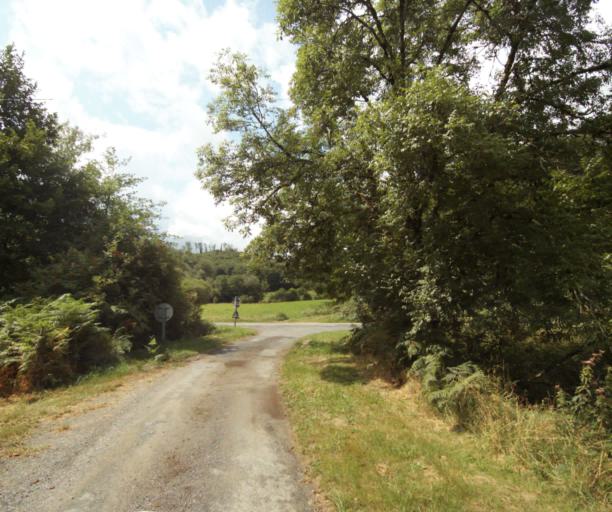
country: FR
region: Limousin
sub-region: Departement de la Correze
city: Sainte-Fortunade
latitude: 45.1717
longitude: 1.7835
